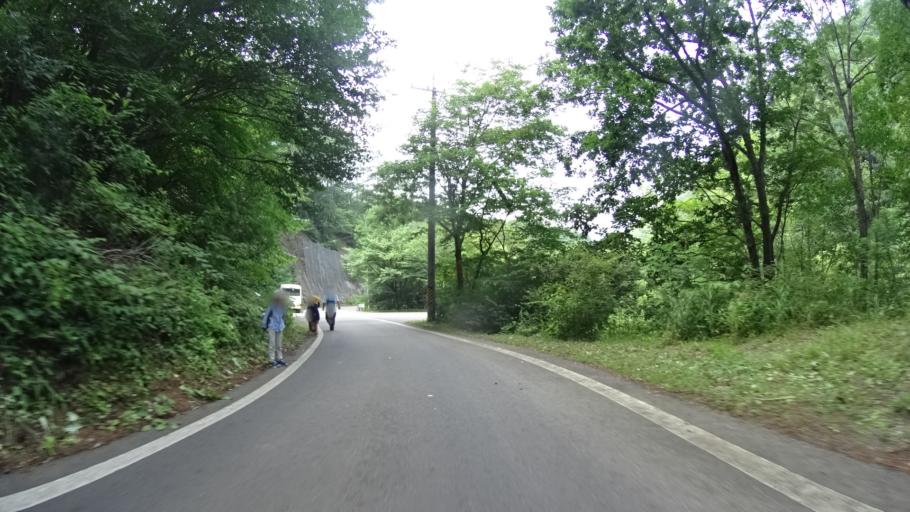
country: JP
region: Nagano
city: Saku
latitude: 36.1164
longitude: 138.6161
